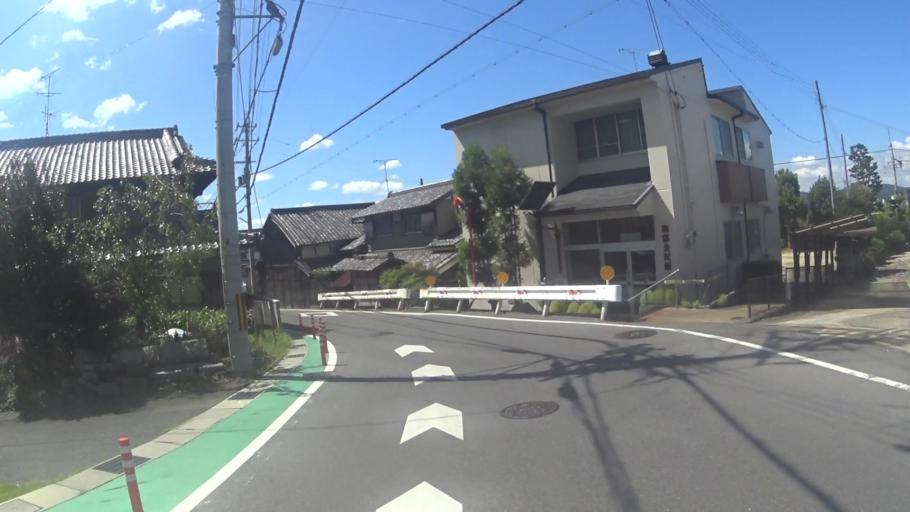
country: JP
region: Kyoto
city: Tanabe
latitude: 34.8146
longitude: 135.8084
